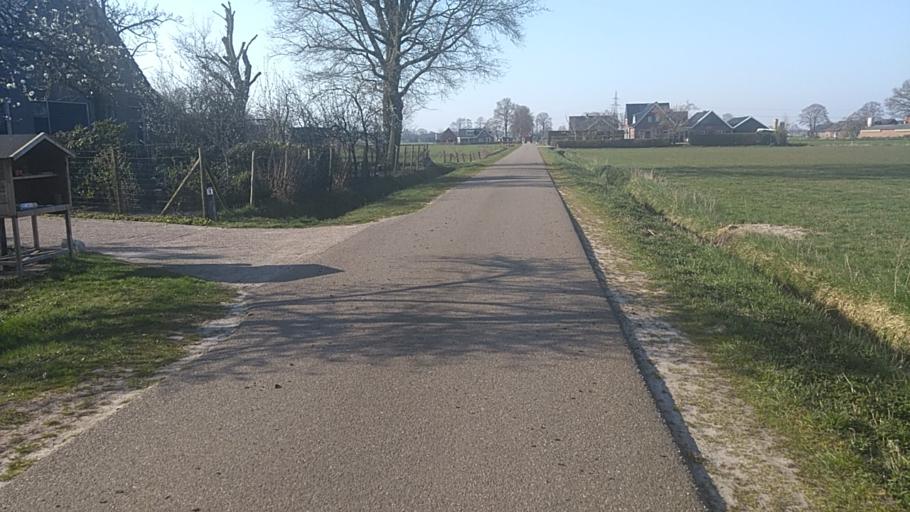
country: NL
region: Overijssel
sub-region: Gemeente Almelo
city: Almelo
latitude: 52.3895
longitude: 6.7030
